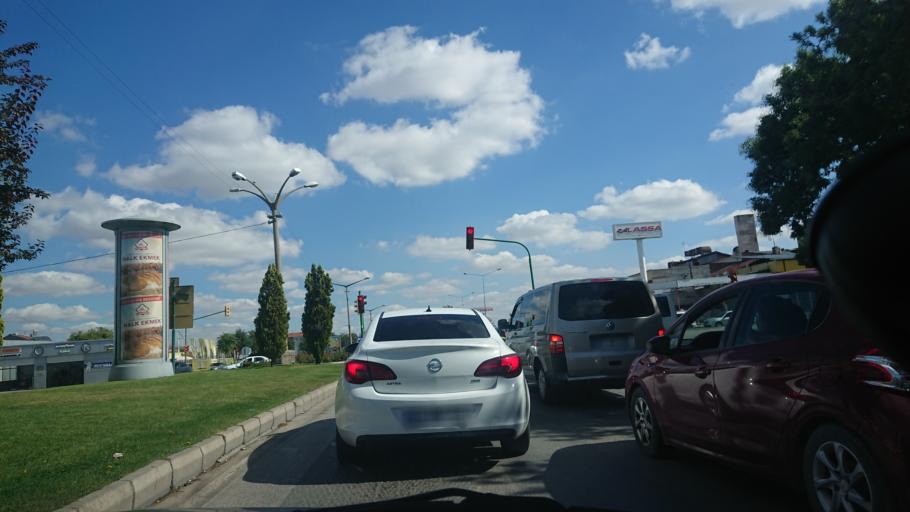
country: TR
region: Eskisehir
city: Eskisehir
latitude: 39.7633
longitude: 30.5588
